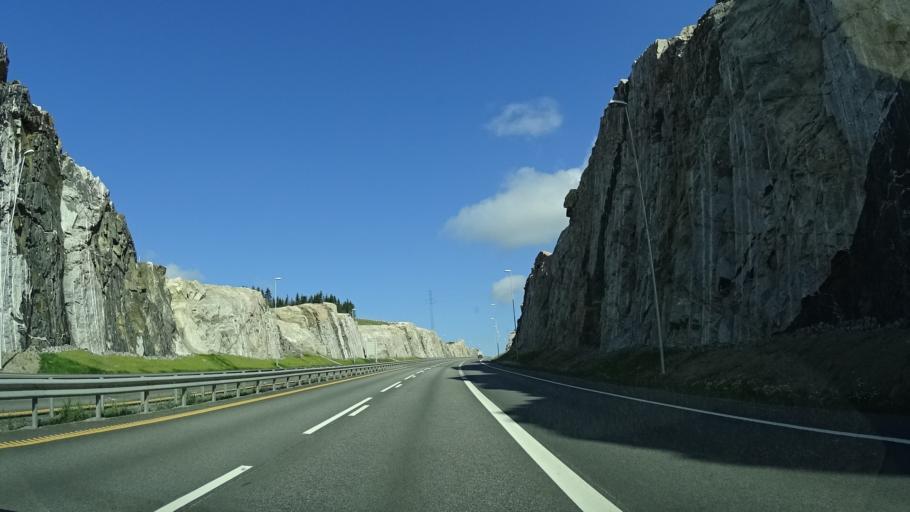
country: NO
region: Ostfold
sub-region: Hobol
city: Elvestad
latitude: 59.6301
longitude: 10.9519
